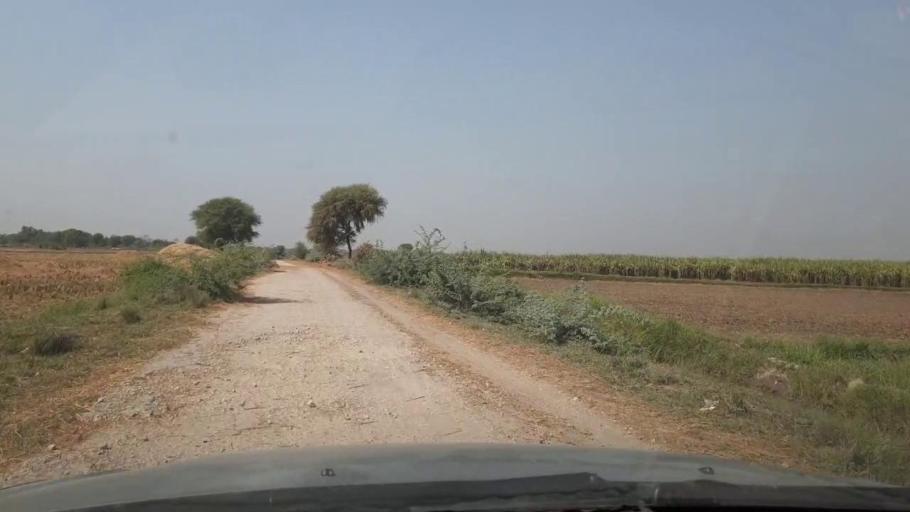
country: PK
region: Sindh
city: Bulri
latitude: 24.8700
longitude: 68.3217
